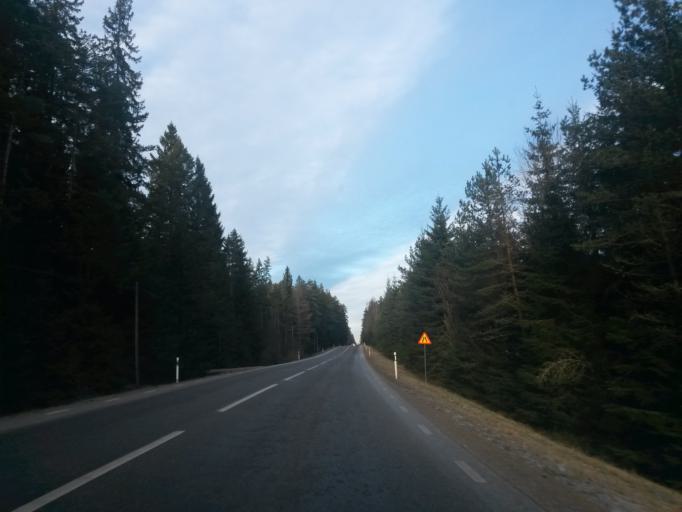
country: SE
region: Vaestra Goetaland
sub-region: Boras Kommun
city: Boras
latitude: 57.8684
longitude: 12.9313
